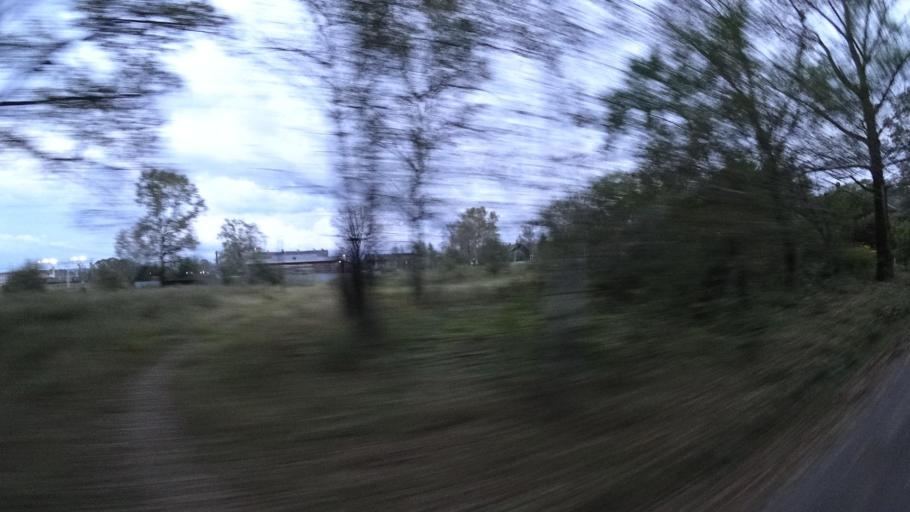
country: RU
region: Jewish Autonomous Oblast
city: Izvestkovyy
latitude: 48.9860
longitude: 131.5463
